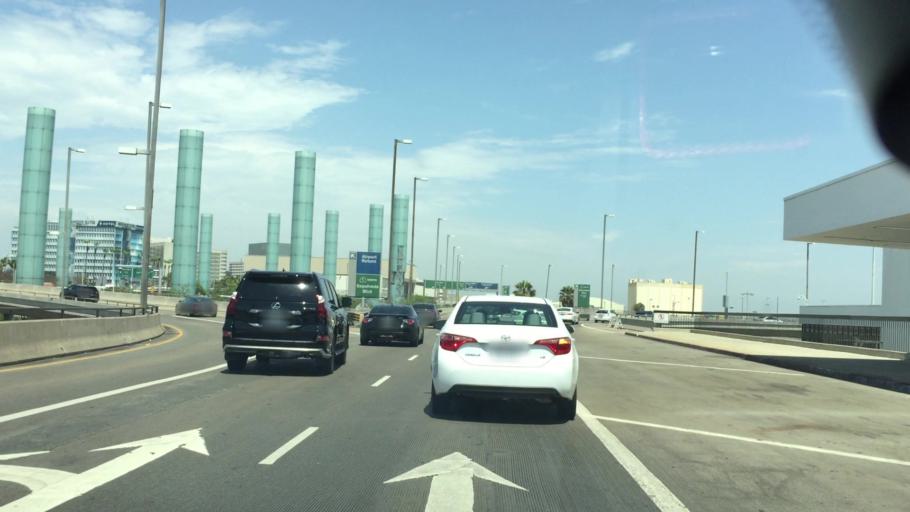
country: US
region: California
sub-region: Los Angeles County
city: El Segundo
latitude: 33.9434
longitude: -118.3983
